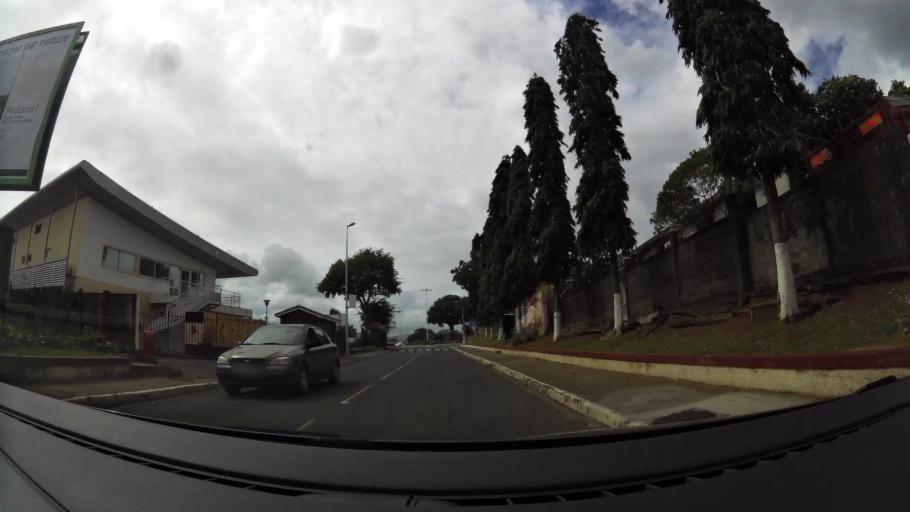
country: GP
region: Guadeloupe
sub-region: Guadeloupe
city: Baie-Mahault
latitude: 16.2620
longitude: -61.5925
